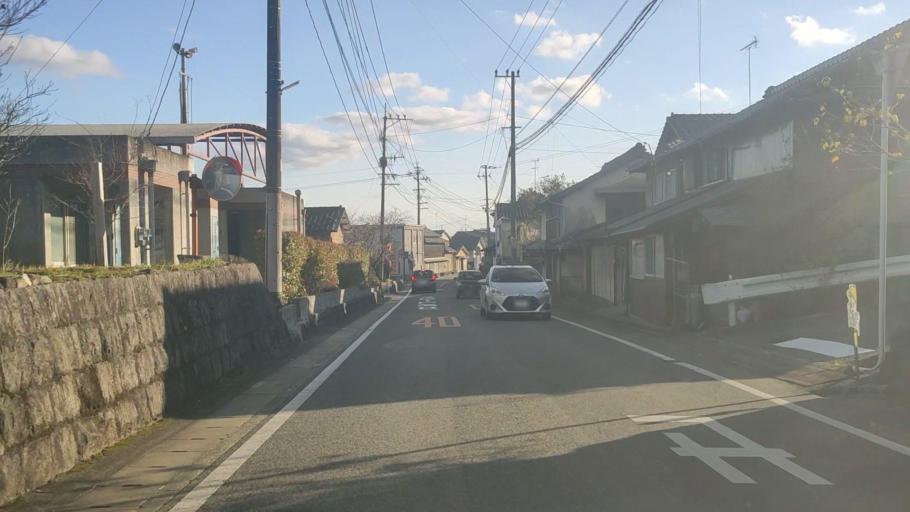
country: JP
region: Saga Prefecture
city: Saga-shi
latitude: 33.3258
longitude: 130.2680
